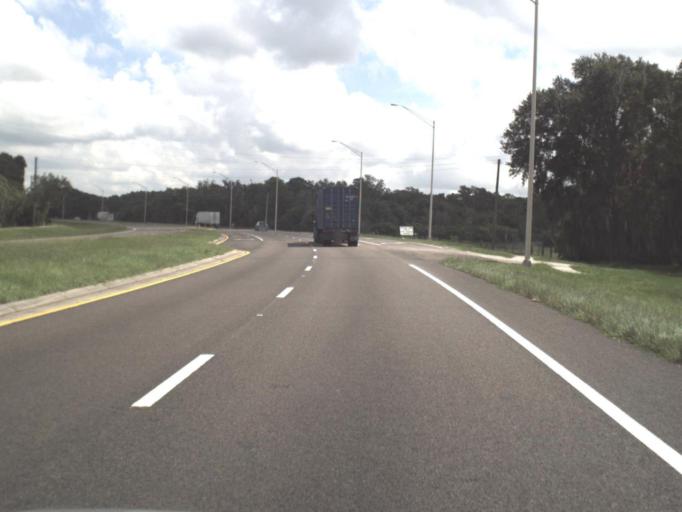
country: US
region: Florida
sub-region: Sarasota County
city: The Meadows
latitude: 27.4768
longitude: -82.4016
